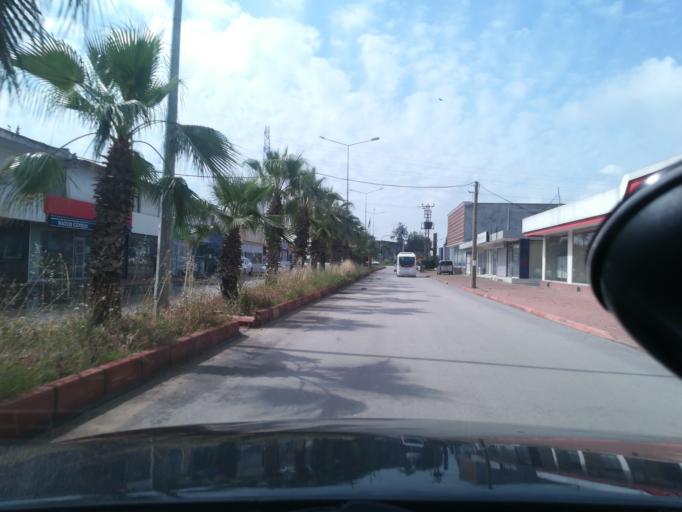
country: TR
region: Adana
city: Yuregir
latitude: 36.9835
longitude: 35.4305
